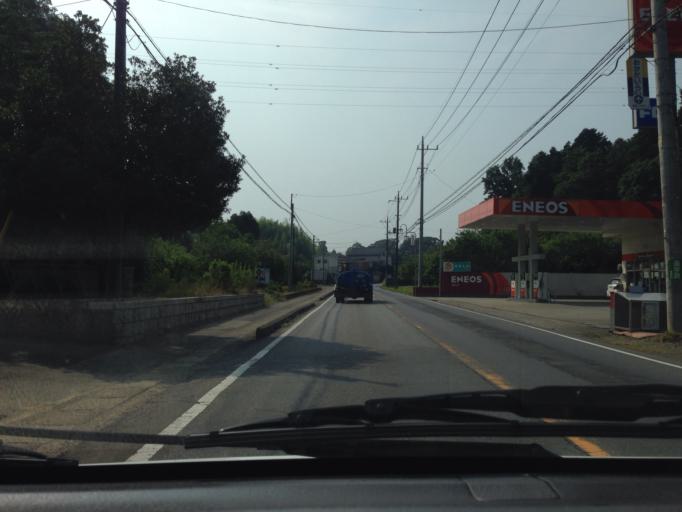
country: JP
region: Ibaraki
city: Inashiki
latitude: 36.0182
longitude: 140.2965
